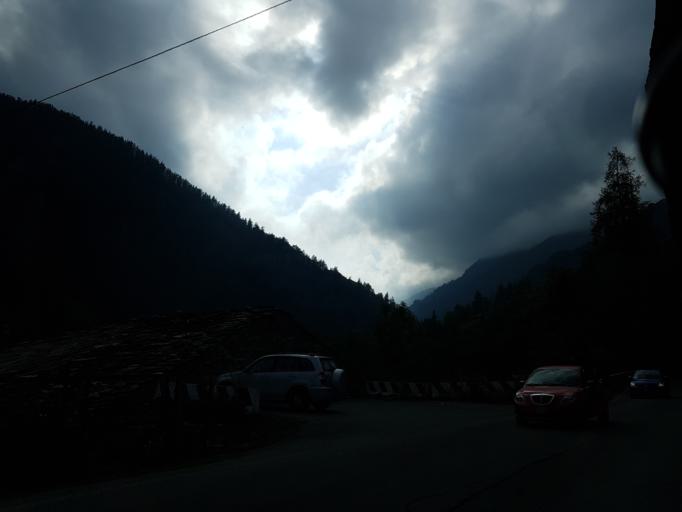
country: IT
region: Piedmont
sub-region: Provincia di Cuneo
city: Casteldelfino
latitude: 44.5855
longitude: 7.0535
